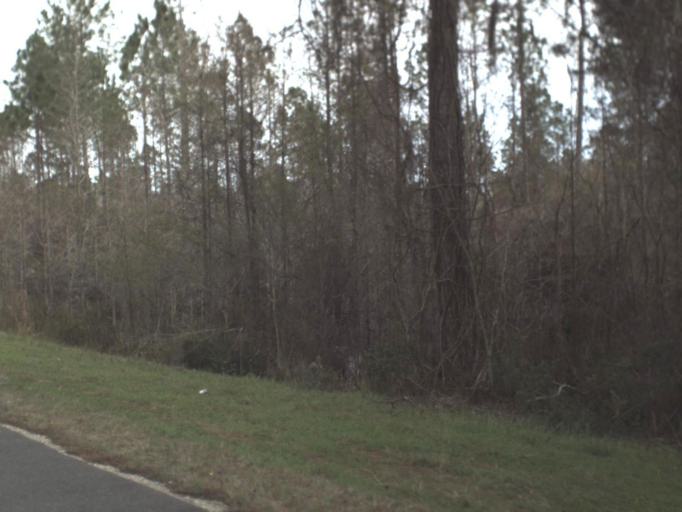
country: US
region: Florida
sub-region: Leon County
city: Woodville
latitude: 30.1876
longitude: -84.0260
